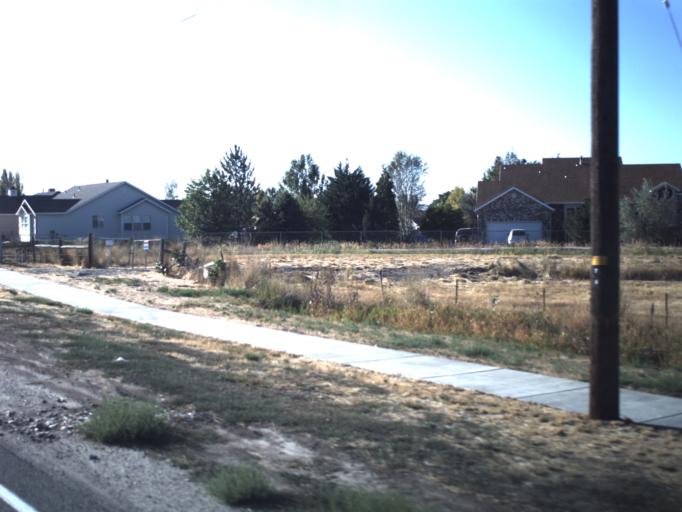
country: US
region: Utah
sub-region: Davis County
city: West Point
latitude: 41.1399
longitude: -112.0940
